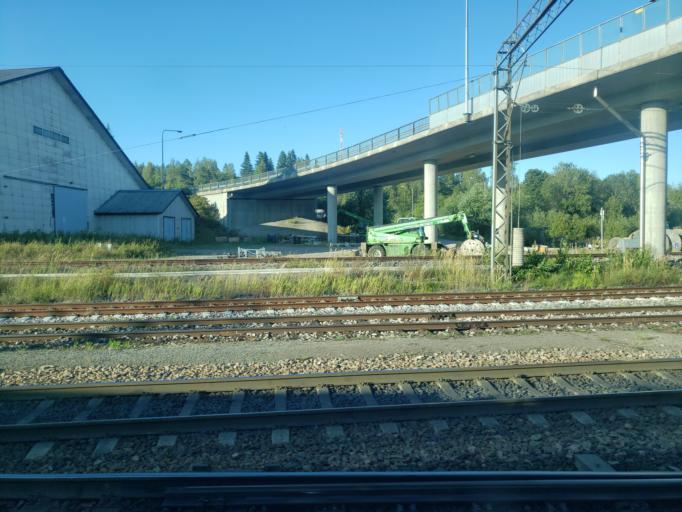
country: FI
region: South Karelia
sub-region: Lappeenranta
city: Lappeenranta
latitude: 60.8651
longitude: 28.2988
